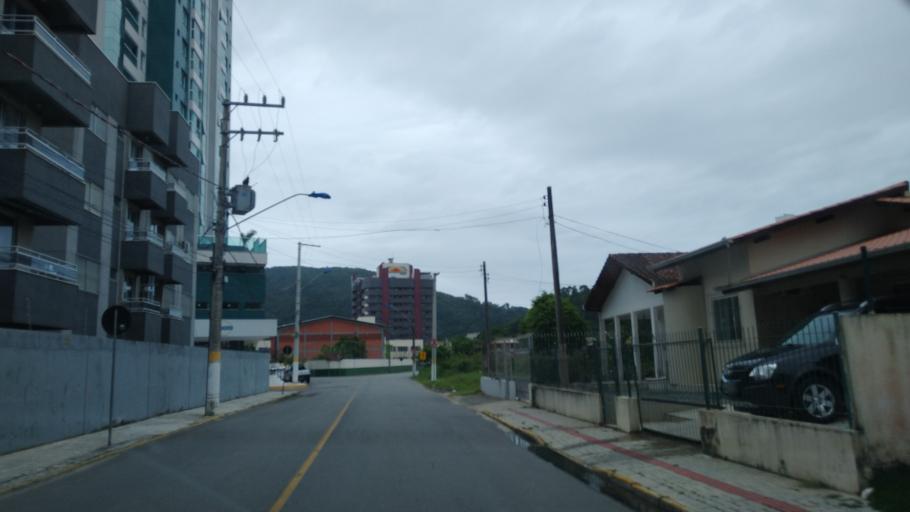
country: BR
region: Santa Catarina
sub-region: Itapema
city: Itapema
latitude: -27.0932
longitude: -48.6120
